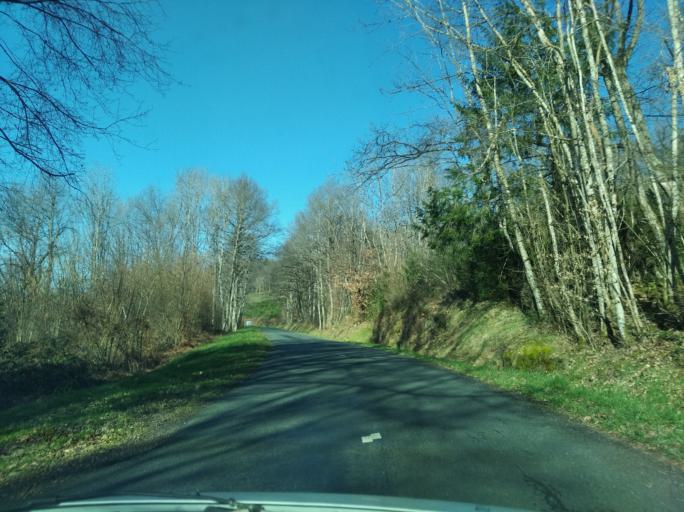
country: FR
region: Auvergne
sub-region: Departement de l'Allier
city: Le Mayet-de-Montagne
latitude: 46.0973
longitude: 3.7519
